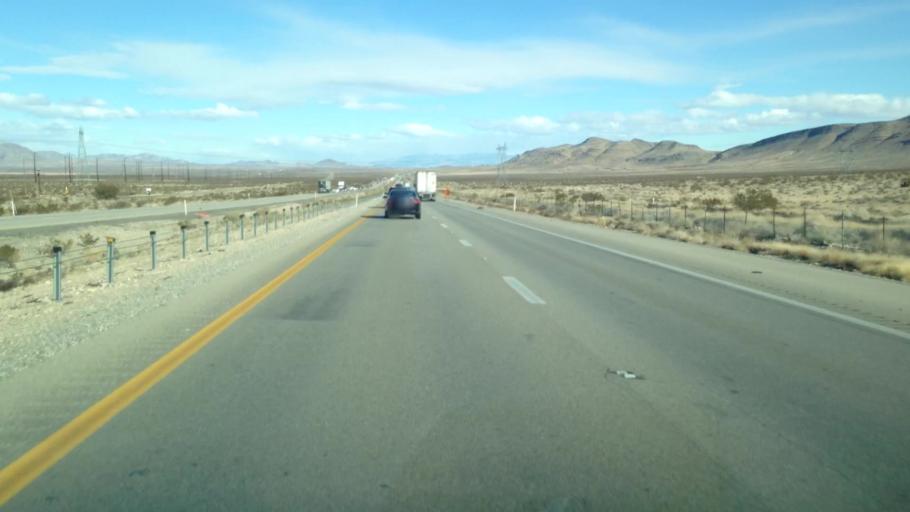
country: US
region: Nevada
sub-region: Clark County
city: Nellis Air Force Base
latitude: 36.3972
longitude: -114.8790
